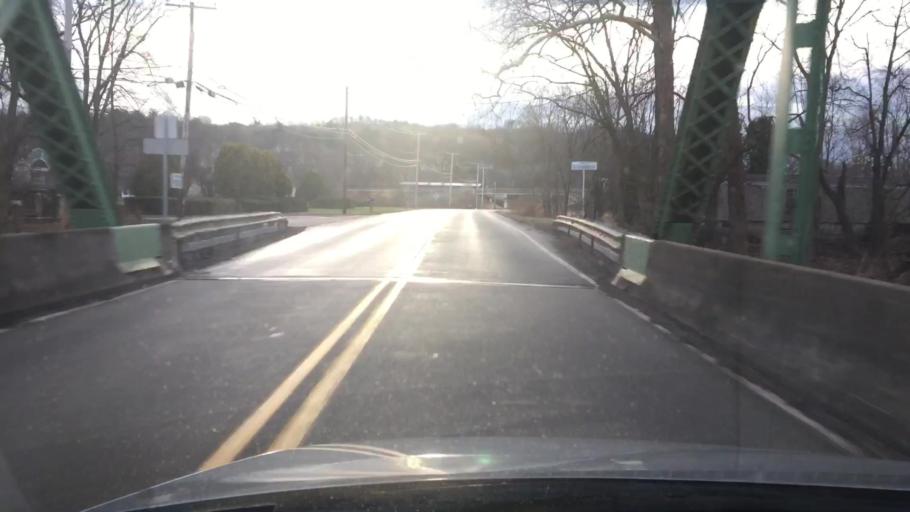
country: US
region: Pennsylvania
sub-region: Columbia County
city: Bloomsburg
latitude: 41.0220
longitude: -76.4734
